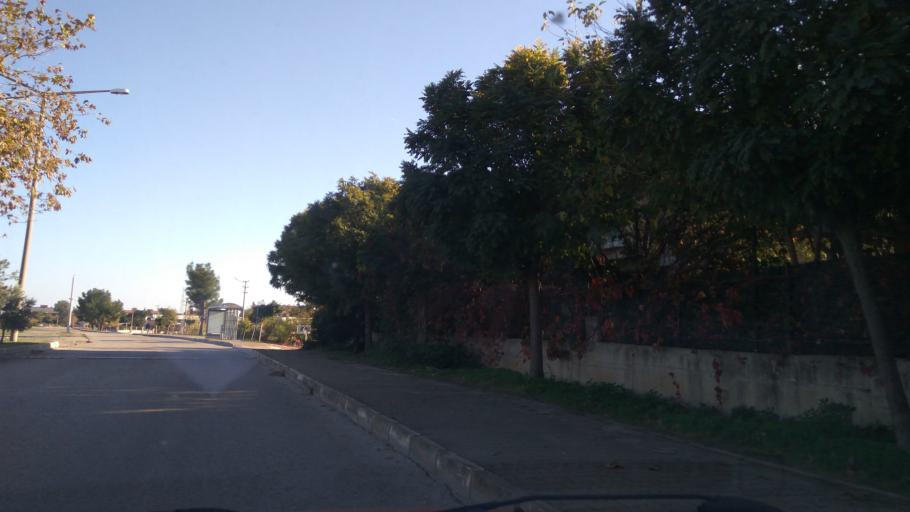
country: TR
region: Antalya
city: Kemer
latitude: 36.5686
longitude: 30.5610
